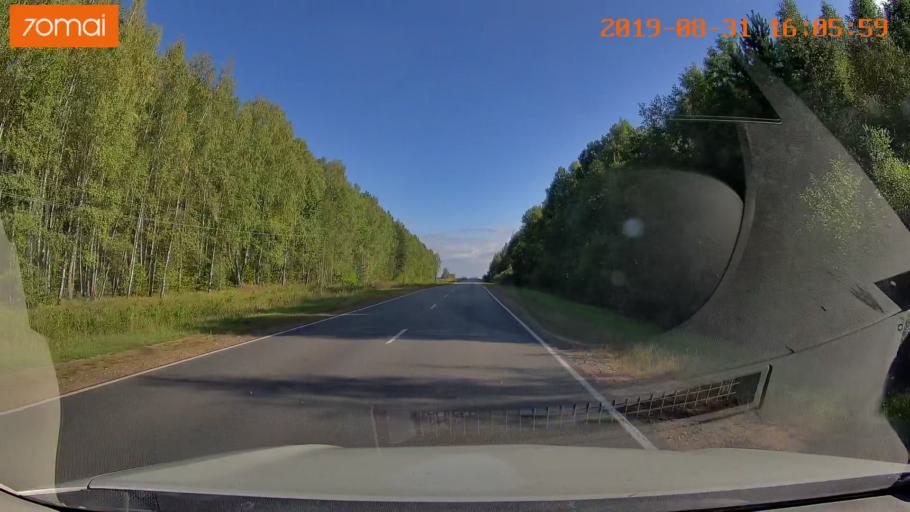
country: RU
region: Kaluga
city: Yukhnov
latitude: 54.6308
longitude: 35.3411
